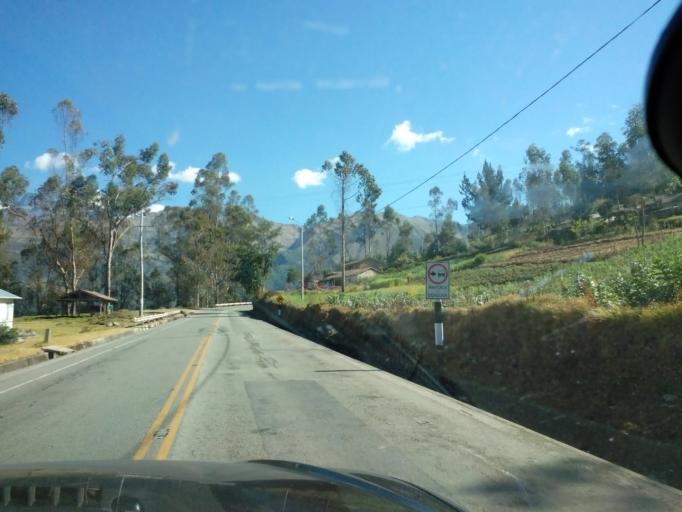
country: PE
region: Apurimac
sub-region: Provincia de Abancay
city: Tamburco
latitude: -13.5939
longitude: -72.8418
